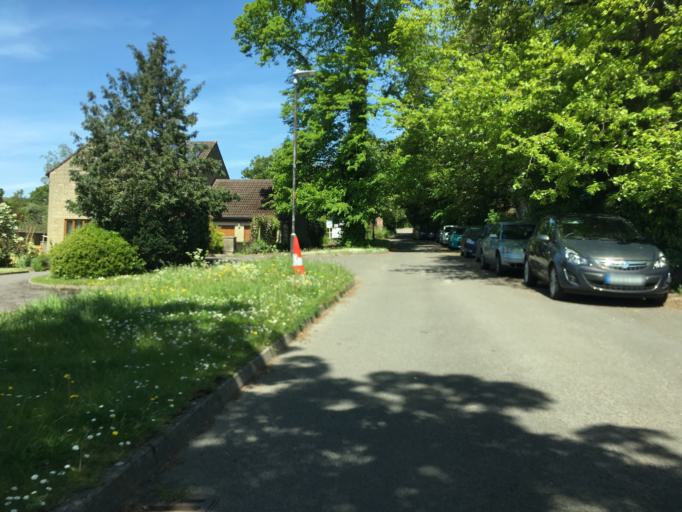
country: GB
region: England
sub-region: Gloucestershire
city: Stroud
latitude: 51.7484
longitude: -2.2180
